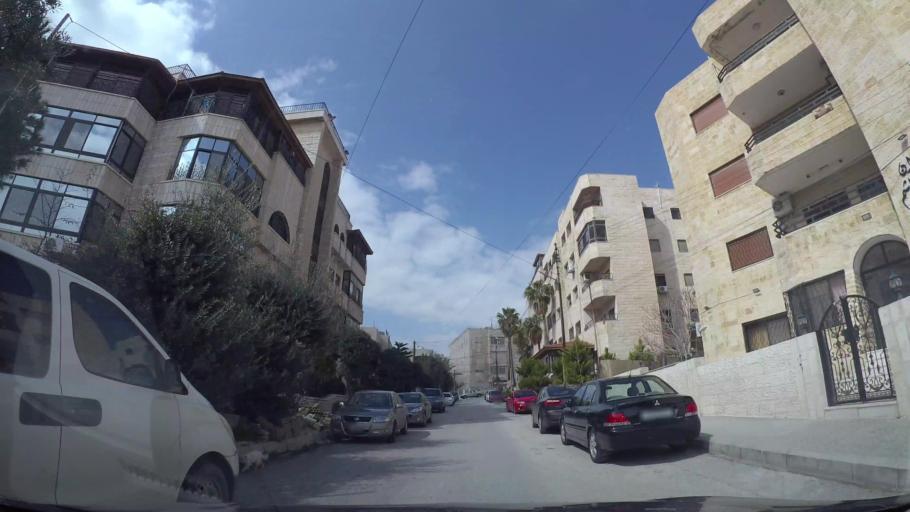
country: JO
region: Amman
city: Amman
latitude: 31.9808
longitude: 35.8984
